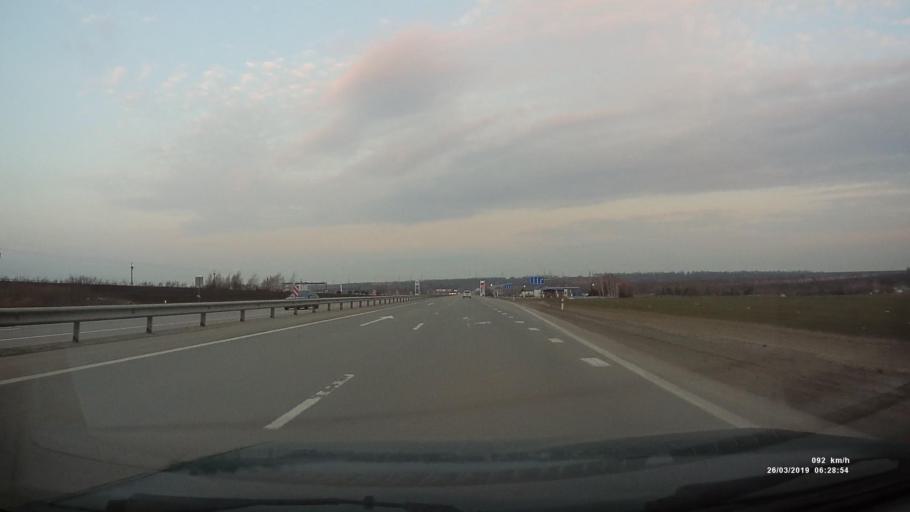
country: RU
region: Rostov
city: Kalinin
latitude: 47.2662
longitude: 39.5841
